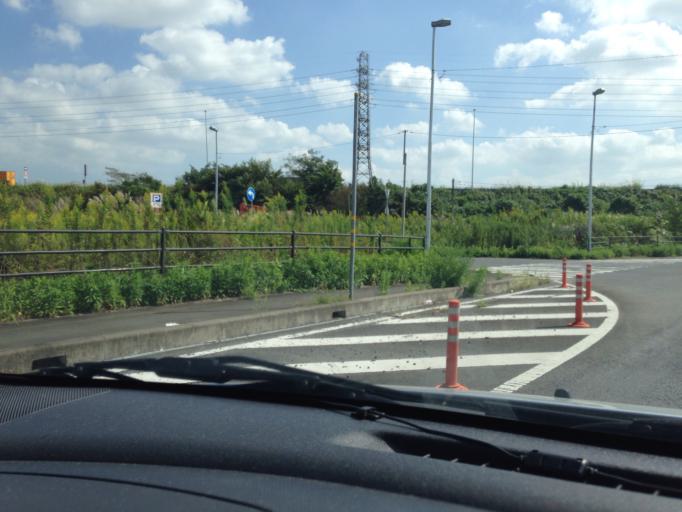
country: JP
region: Ibaraki
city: Mito-shi
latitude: 36.4178
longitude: 140.4243
